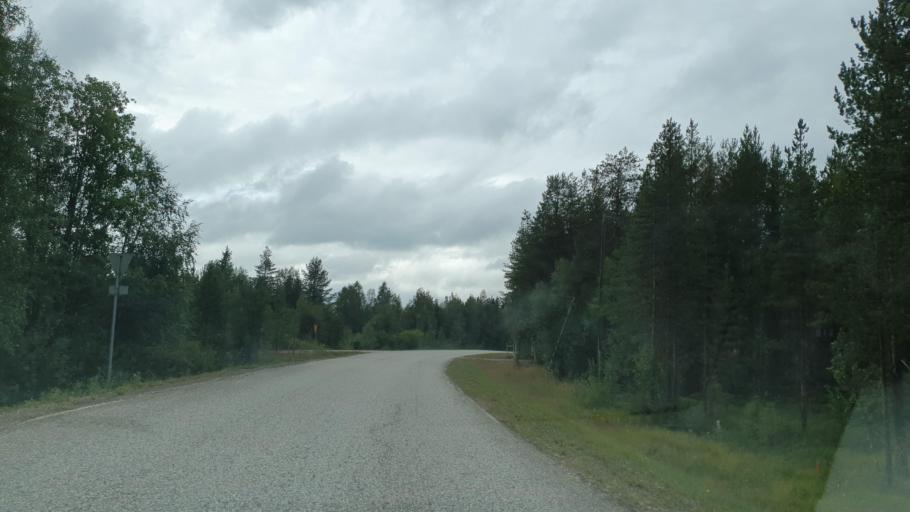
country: FI
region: Lapland
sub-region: Tunturi-Lappi
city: Kolari
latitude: 67.5038
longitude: 24.2664
